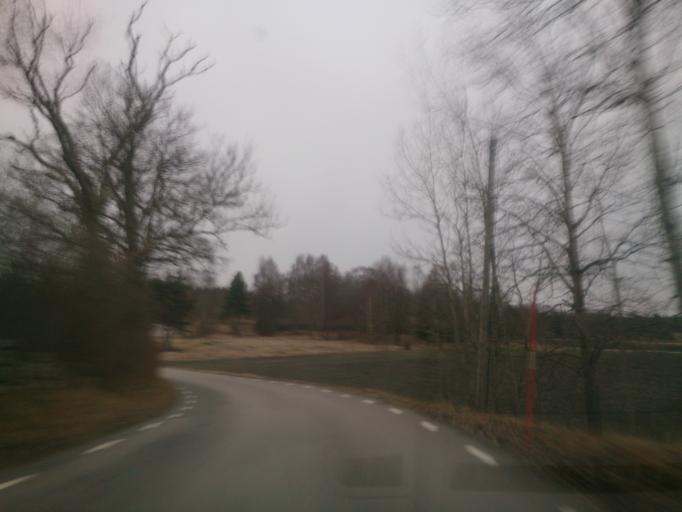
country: SE
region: OEstergoetland
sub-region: Norrkopings Kommun
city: Krokek
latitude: 58.5028
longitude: 16.5805
